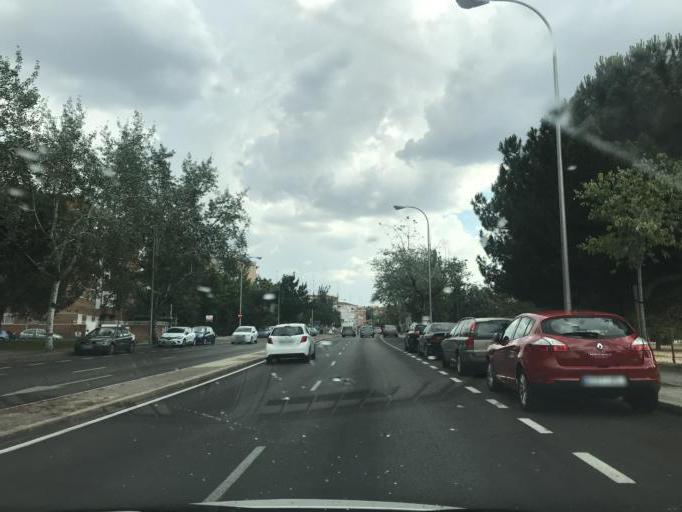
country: ES
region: Madrid
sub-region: Provincia de Madrid
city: Pinar de Chamartin
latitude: 40.4748
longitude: -3.6556
